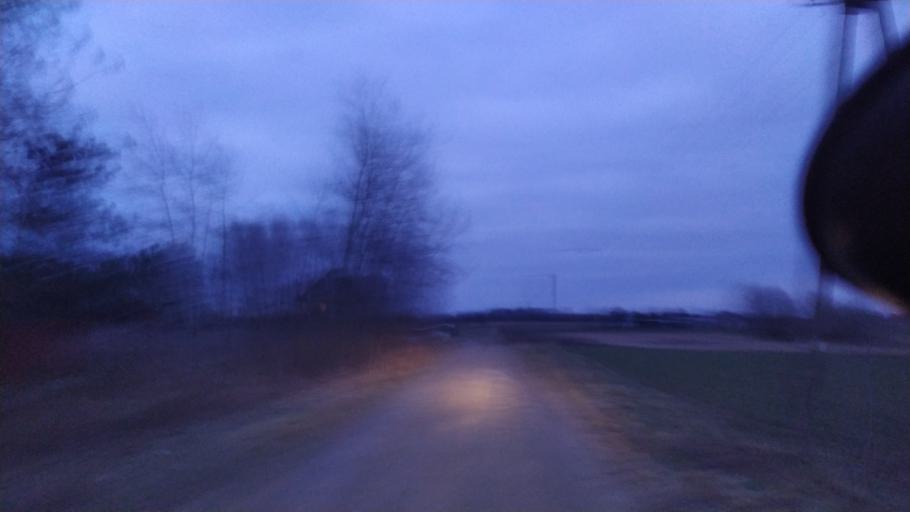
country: PL
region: Lublin Voivodeship
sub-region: Powiat lubartowski
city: Kamionka
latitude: 51.3935
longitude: 22.4220
